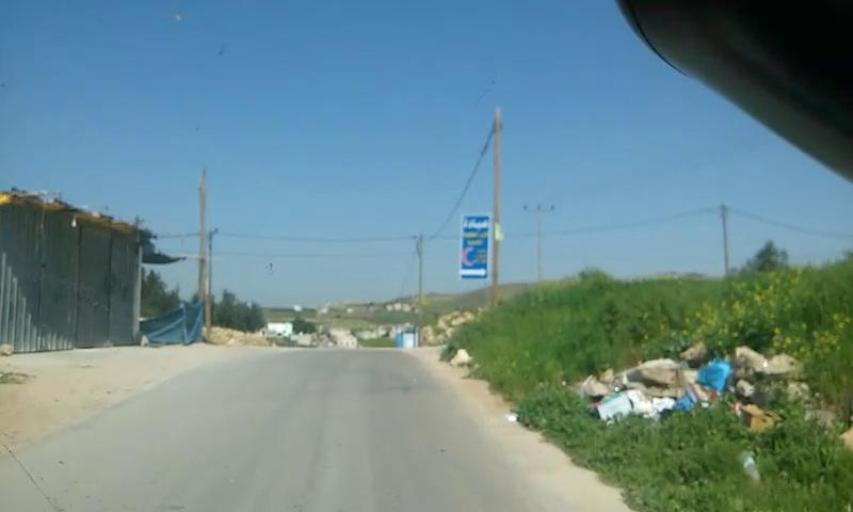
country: PS
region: West Bank
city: Al Majd
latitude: 31.4756
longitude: 34.9507
